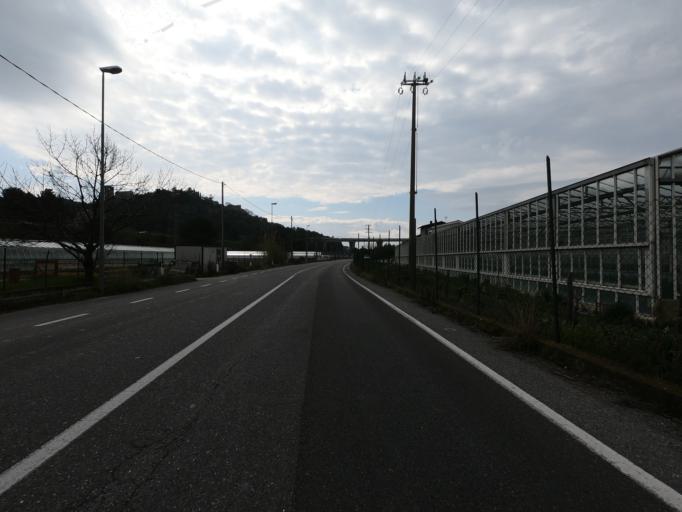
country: IT
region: Liguria
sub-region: Provincia di Savona
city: Andora
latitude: 43.9692
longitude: 8.1406
